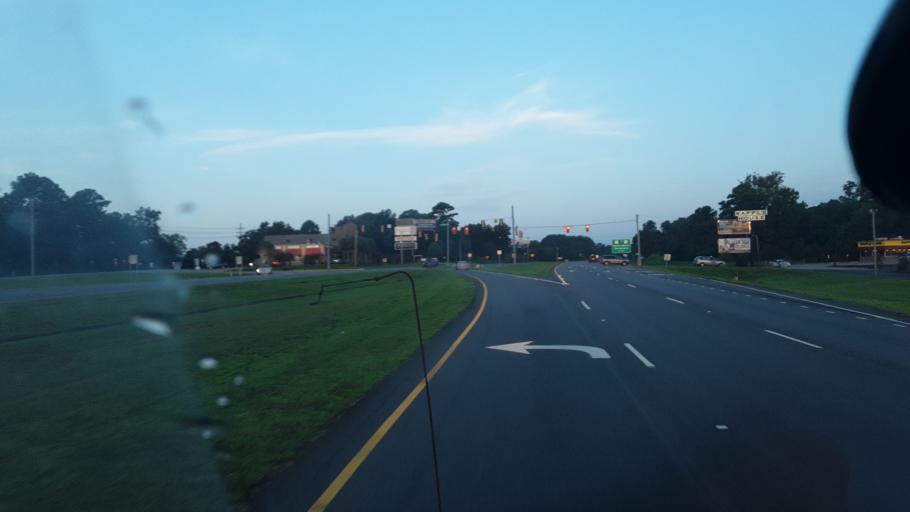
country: US
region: South Carolina
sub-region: Horry County
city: Little River
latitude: 33.8652
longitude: -78.6440
